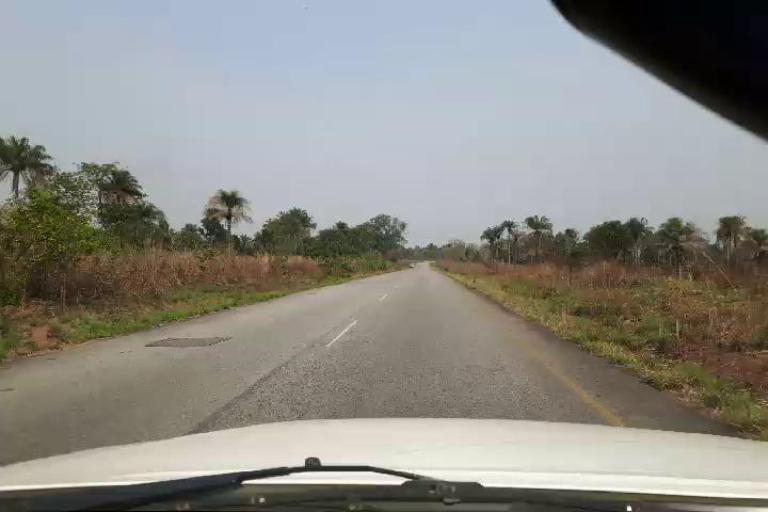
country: SL
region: Southern Province
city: Largo
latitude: 8.3070
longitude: -12.2060
